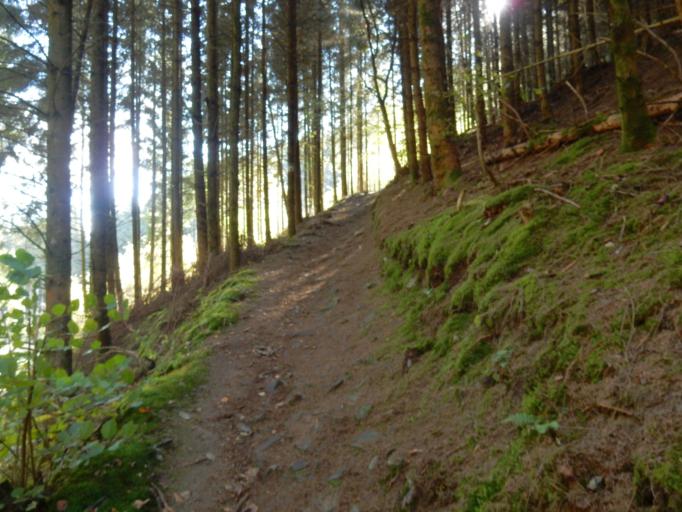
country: LU
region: Diekirch
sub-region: Canton de Wiltz
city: Bavigne
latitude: 49.9137
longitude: 5.8868
